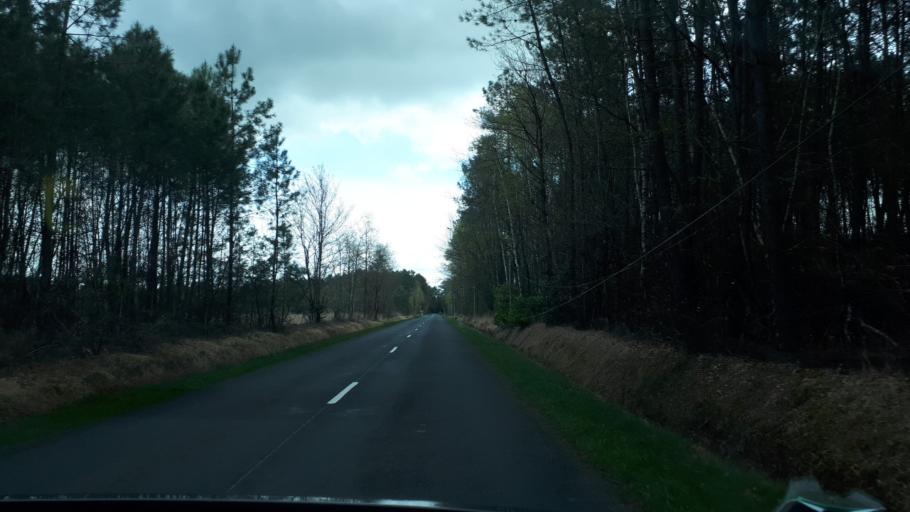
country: FR
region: Pays de la Loire
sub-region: Departement de la Sarthe
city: Le Grand-Luce
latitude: 47.8757
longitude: 0.4171
